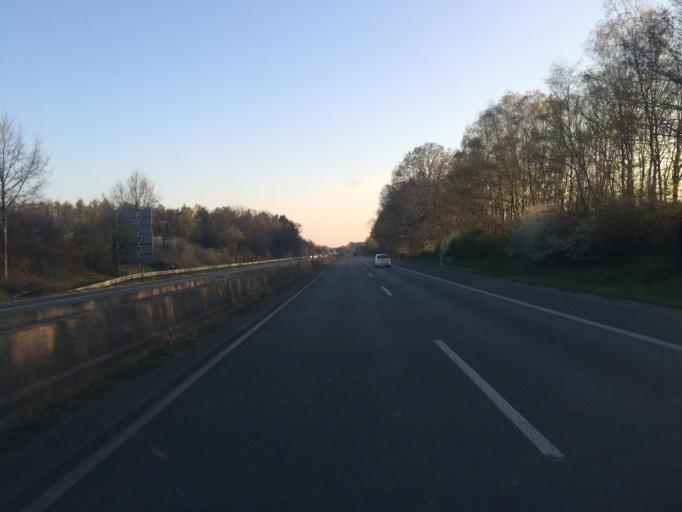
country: DE
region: North Rhine-Westphalia
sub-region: Regierungsbezirk Munster
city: Heiden
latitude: 51.8035
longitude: 6.9805
